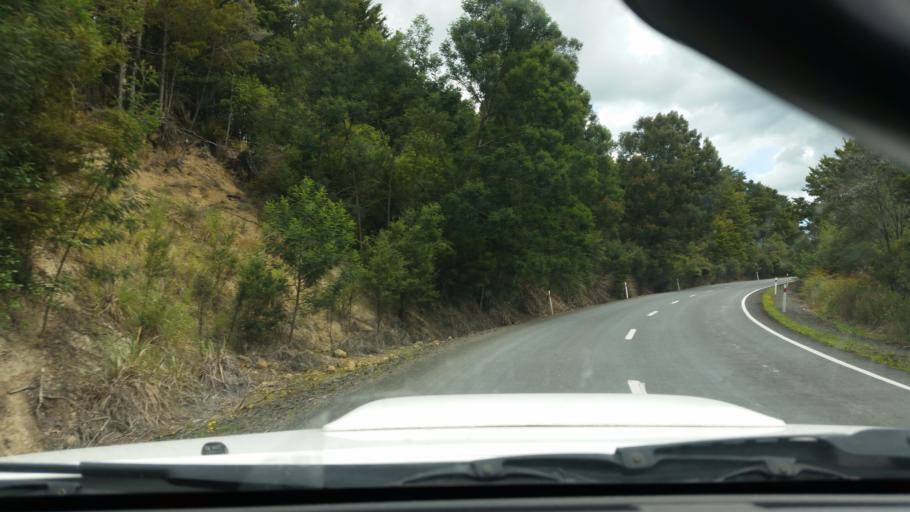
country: NZ
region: Northland
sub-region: Kaipara District
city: Dargaville
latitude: -35.7787
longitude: 173.9073
